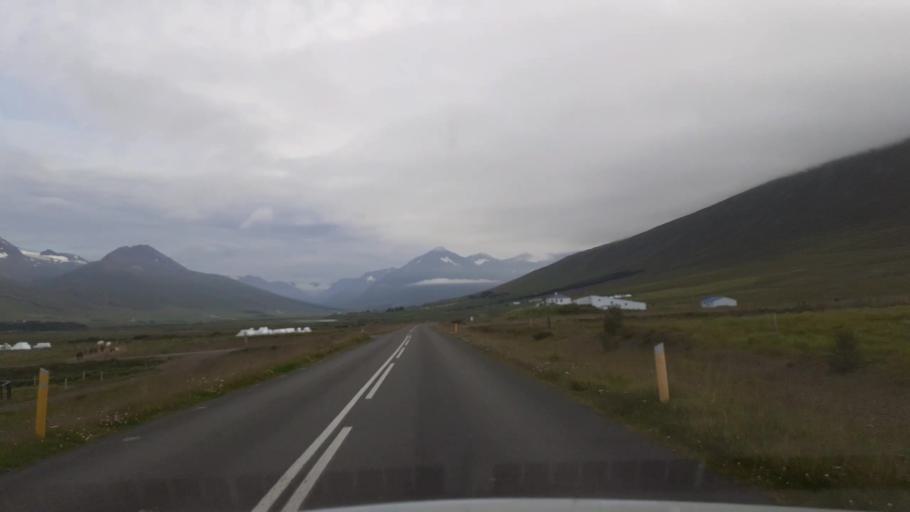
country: IS
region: Northeast
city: Dalvik
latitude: 65.9496
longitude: -18.5550
